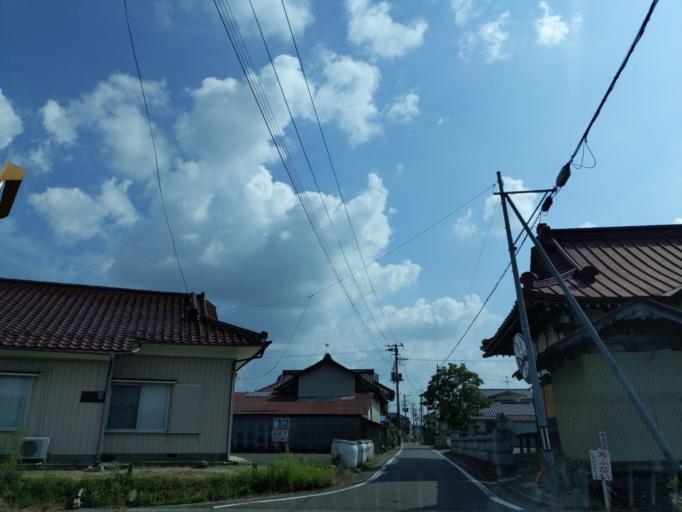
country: JP
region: Fukushima
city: Sukagawa
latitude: 37.3320
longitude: 140.3246
